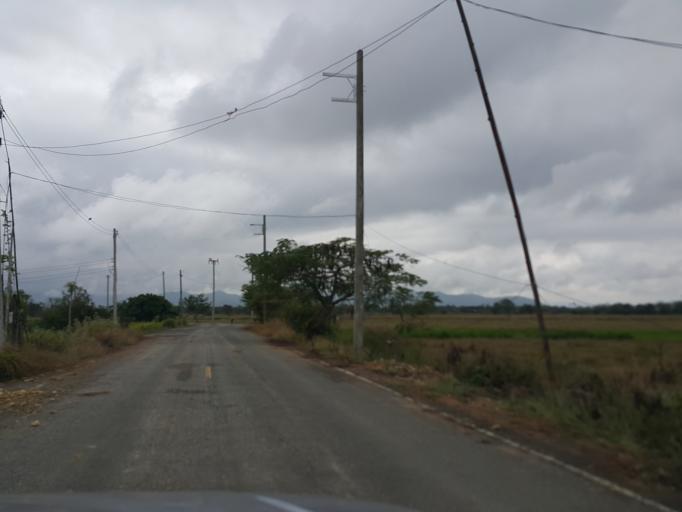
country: TH
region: Lamphun
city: Ban Thi
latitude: 18.6838
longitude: 99.1352
